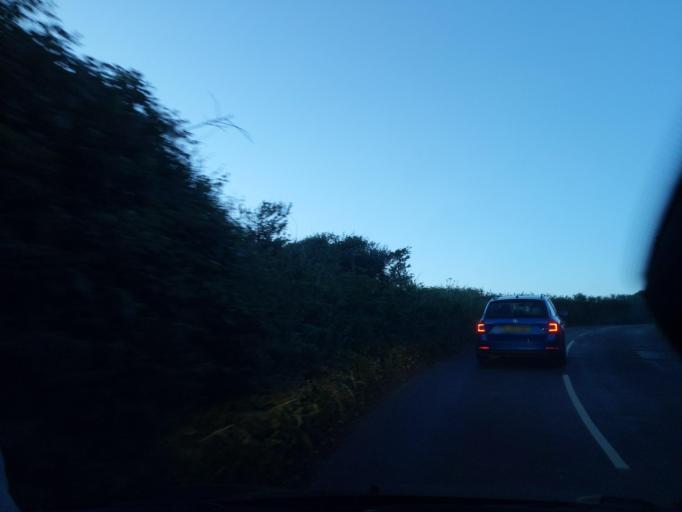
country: GB
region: England
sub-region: Cornwall
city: St. Buryan
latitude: 50.0912
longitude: -5.5985
